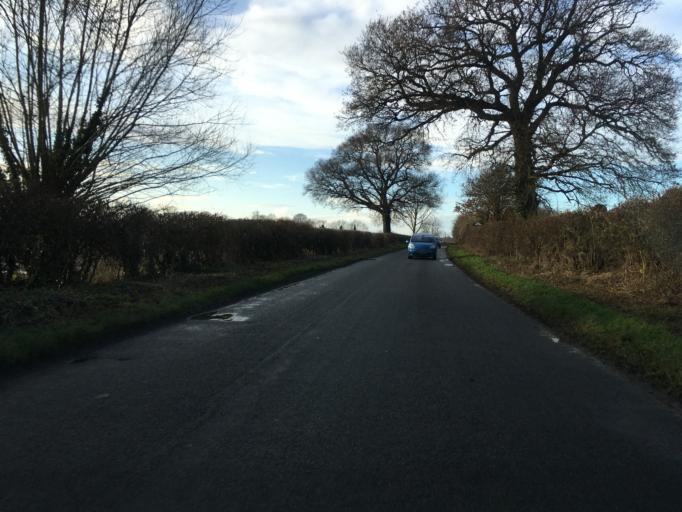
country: GB
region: England
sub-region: Warwickshire
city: Alcester
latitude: 52.2236
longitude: -1.8054
